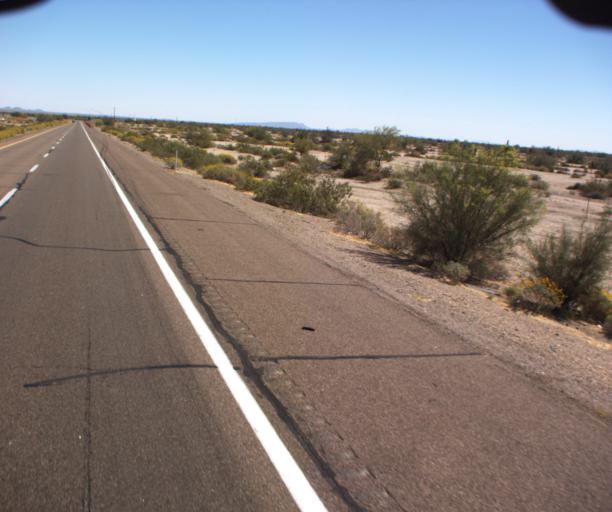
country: US
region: Arizona
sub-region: Yuma County
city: Wellton
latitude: 32.7298
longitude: -113.7249
